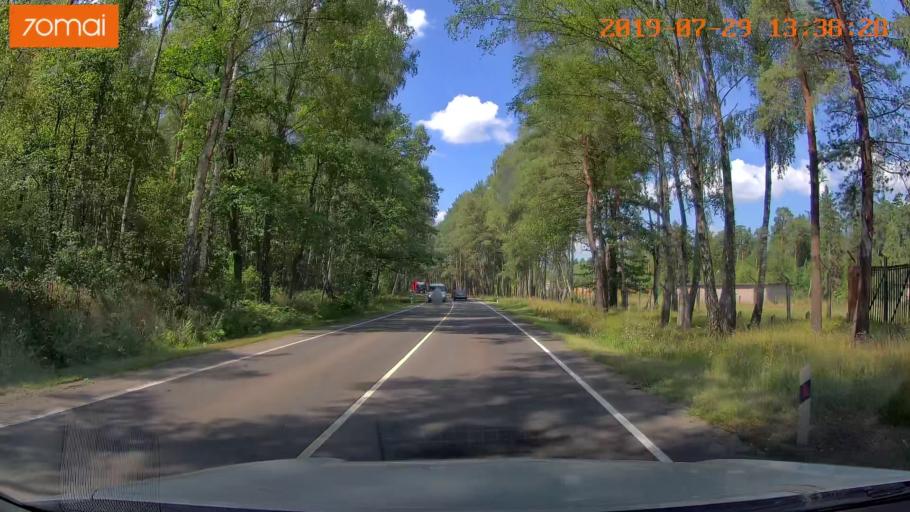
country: RU
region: Kaliningrad
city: Volochayevskoye
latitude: 54.7213
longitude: 20.1705
